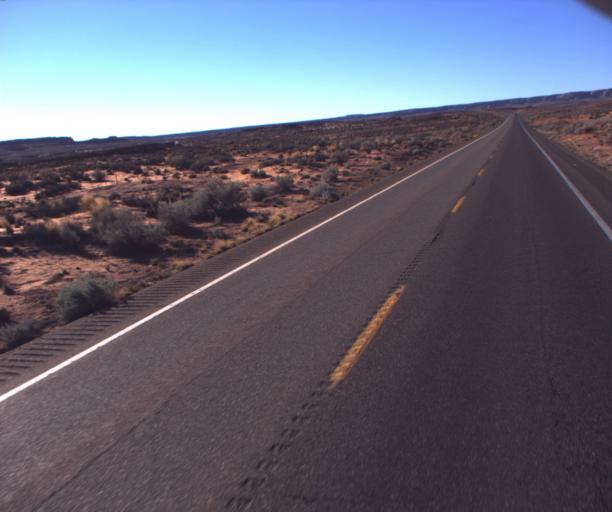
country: US
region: Arizona
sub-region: Coconino County
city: LeChee
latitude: 36.8578
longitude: -111.5061
